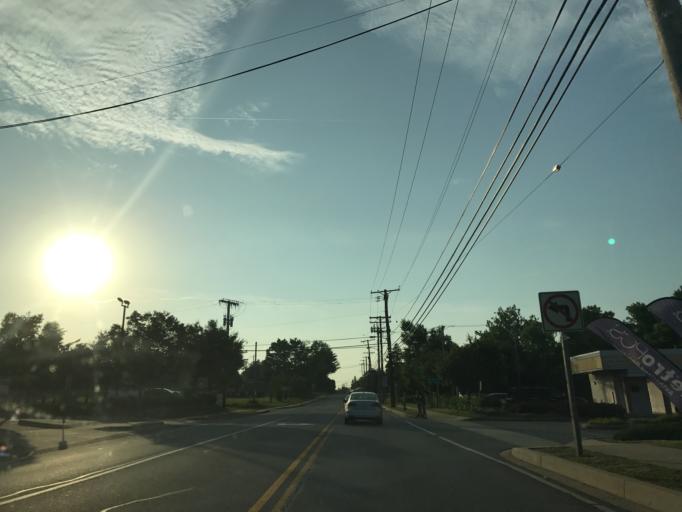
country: US
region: Maryland
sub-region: Harford County
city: Edgewood
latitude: 39.4270
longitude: -76.2995
